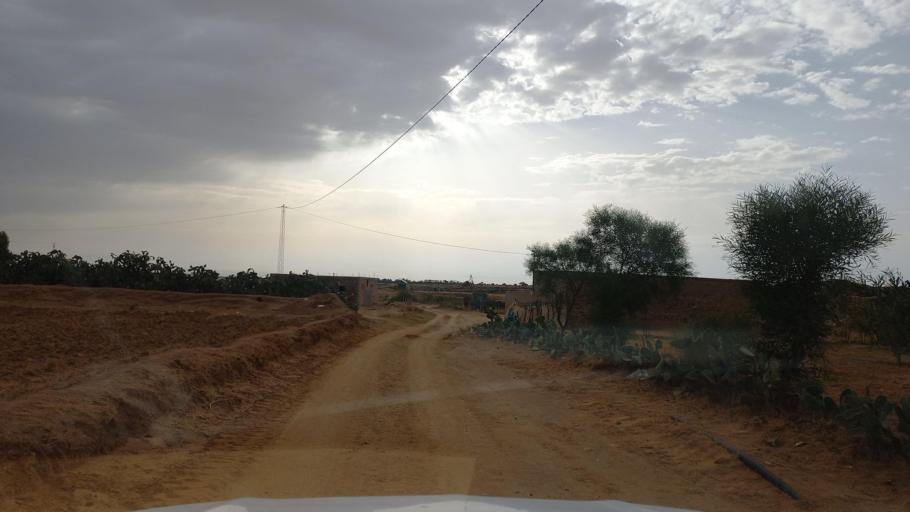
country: TN
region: Al Qasrayn
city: Kasserine
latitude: 35.1878
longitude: 9.0545
